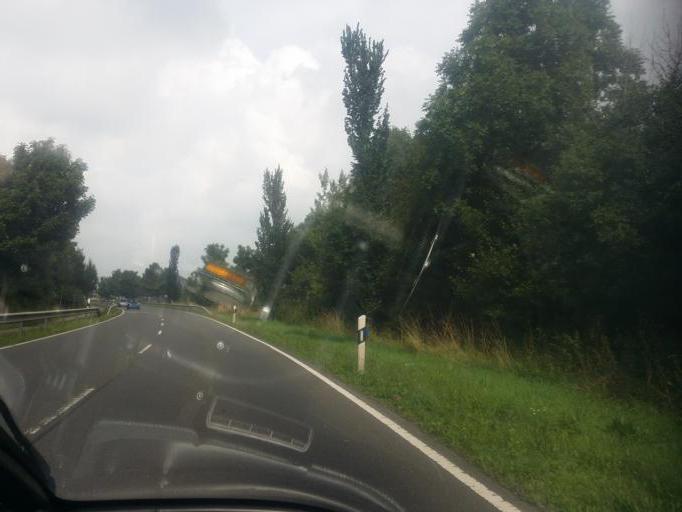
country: DE
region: Schleswig-Holstein
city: Heide
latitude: 54.1913
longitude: 9.1225
